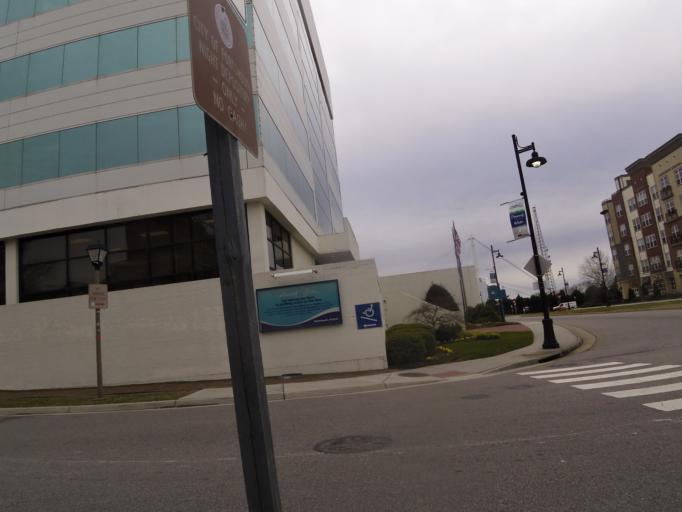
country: US
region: Virginia
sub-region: City of Portsmouth
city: Portsmouth
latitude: 36.8331
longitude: -76.2976
